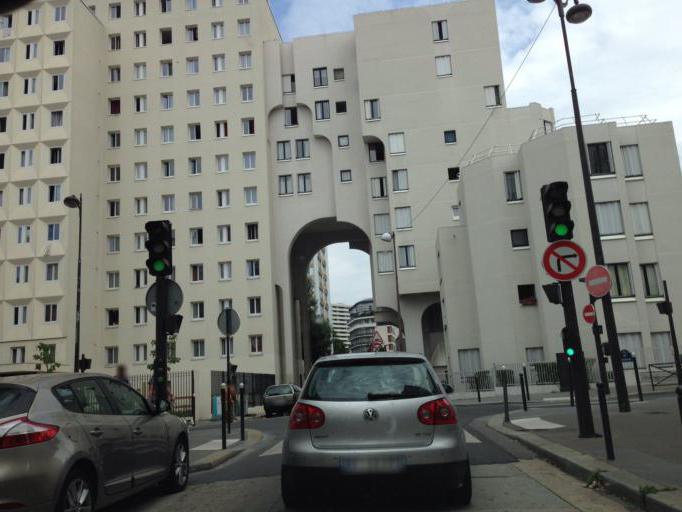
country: FR
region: Ile-de-France
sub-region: Departement des Hauts-de-Seine
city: Malakoff
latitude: 48.8356
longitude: 2.3112
